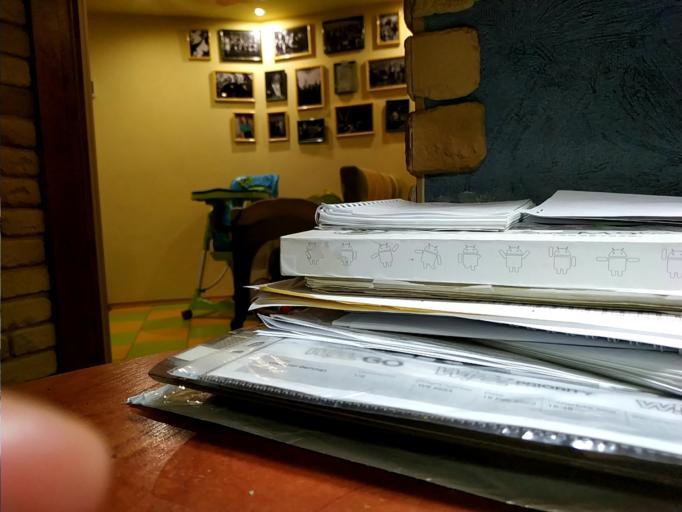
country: RU
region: Arkhangelskaya
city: Konevo
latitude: 62.1975
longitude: 38.9124
